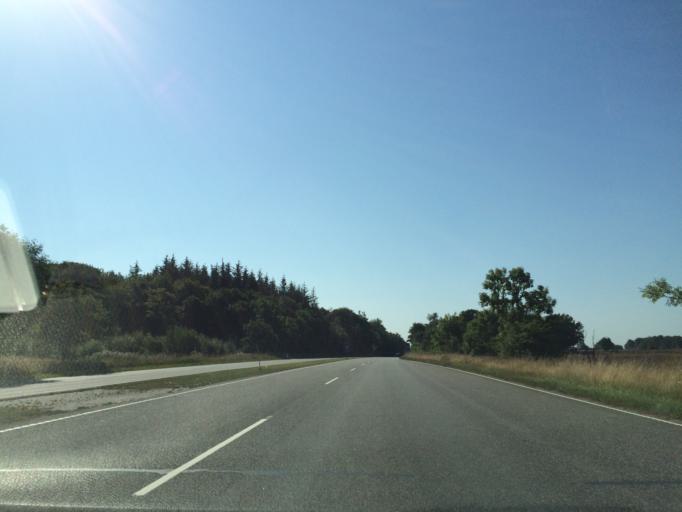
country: DK
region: South Denmark
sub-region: Kolding Kommune
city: Kolding
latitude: 55.5191
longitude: 9.5003
